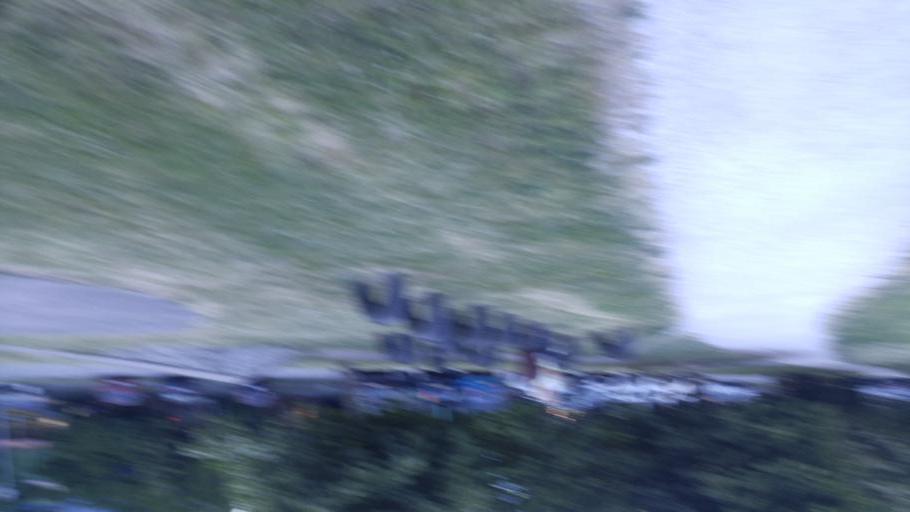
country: HU
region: Budapest
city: Budapest III. keruelet
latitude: 47.5404
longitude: 19.0385
